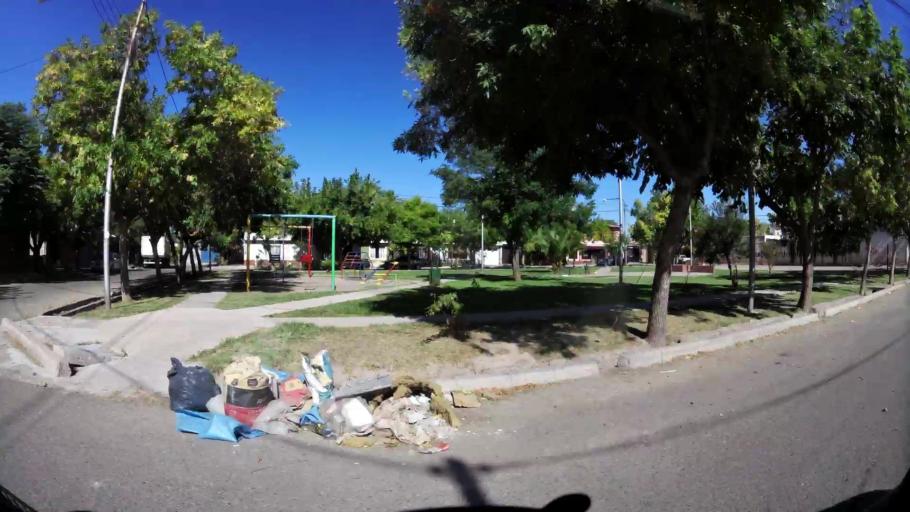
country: AR
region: Mendoza
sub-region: Departamento de Godoy Cruz
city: Godoy Cruz
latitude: -32.9394
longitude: -68.8101
